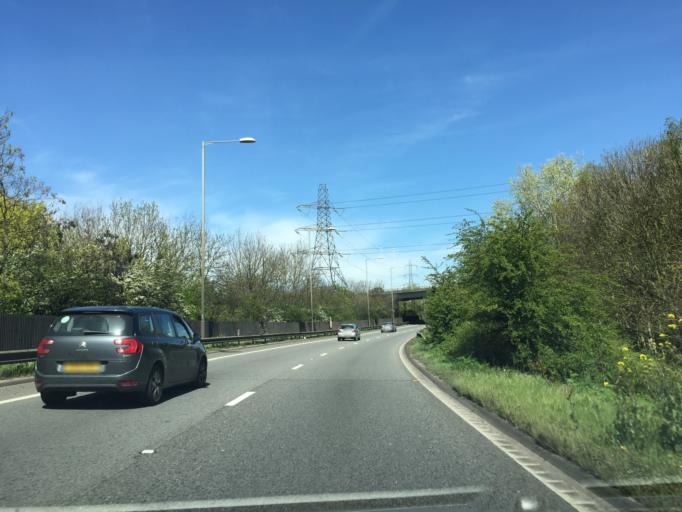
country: GB
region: England
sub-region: Greater London
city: Woodford Green
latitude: 51.5906
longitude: 0.0365
